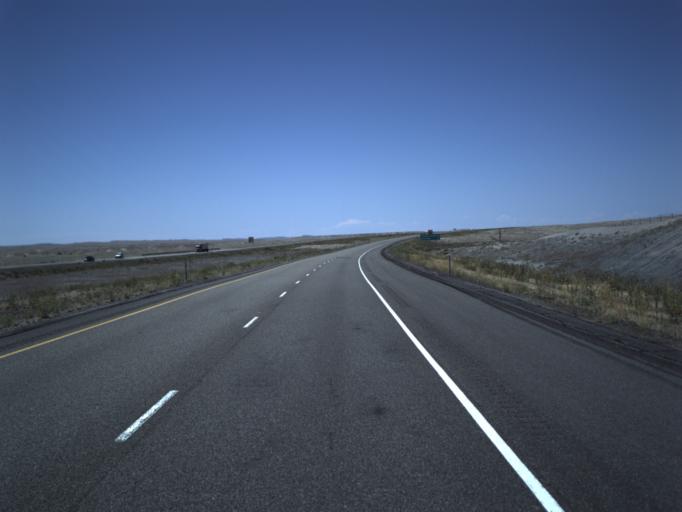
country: US
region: Utah
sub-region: Grand County
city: Moab
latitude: 38.9339
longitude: -109.4217
